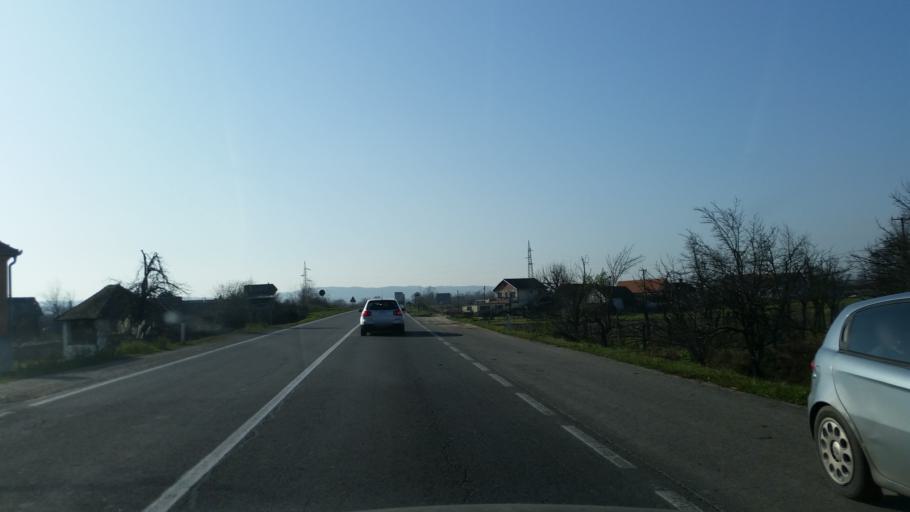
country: RS
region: Central Serbia
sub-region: Belgrade
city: Lazarevac
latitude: 44.4008
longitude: 20.2477
